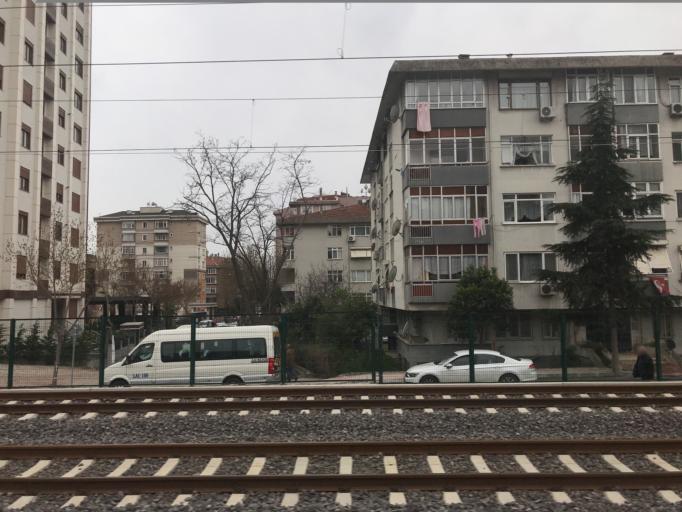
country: TR
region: Istanbul
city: Maltepe
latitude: 40.8966
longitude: 29.1719
